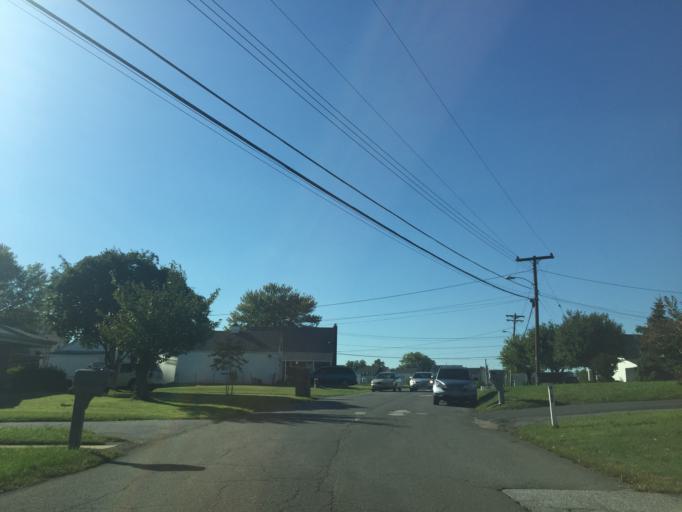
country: US
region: Maryland
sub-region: Baltimore County
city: Rossville
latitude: 39.3628
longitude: -76.4896
